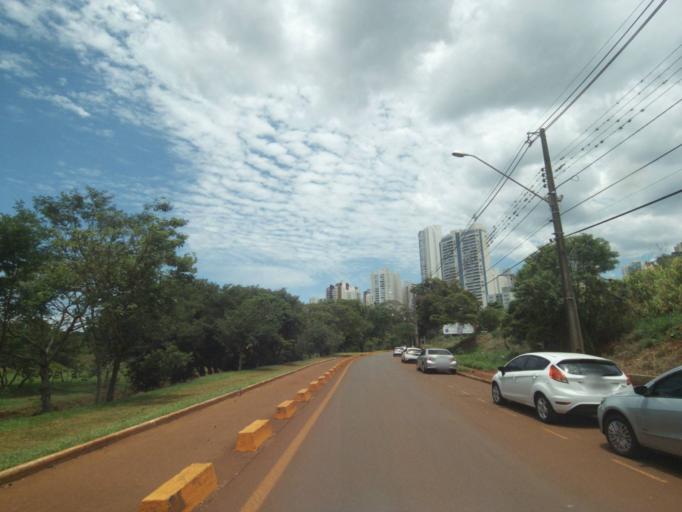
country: BR
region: Parana
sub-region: Londrina
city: Londrina
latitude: -23.3228
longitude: -51.1818
